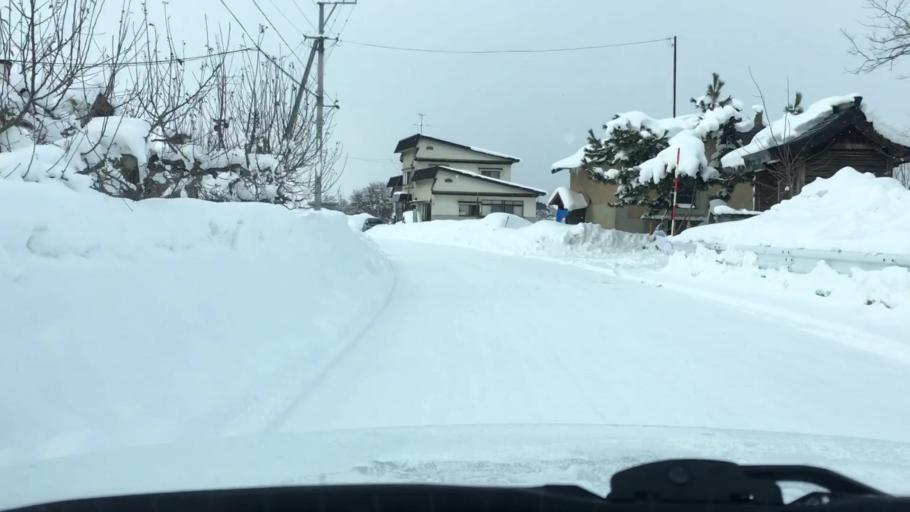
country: JP
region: Aomori
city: Hirosaki
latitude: 40.6535
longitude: 140.4805
